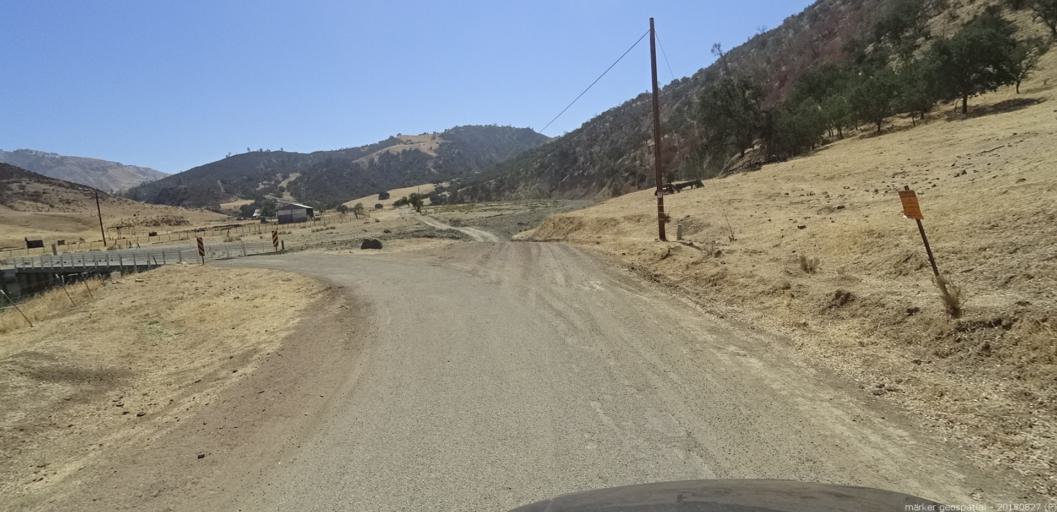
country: US
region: California
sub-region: Monterey County
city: King City
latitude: 36.2933
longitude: -120.8935
